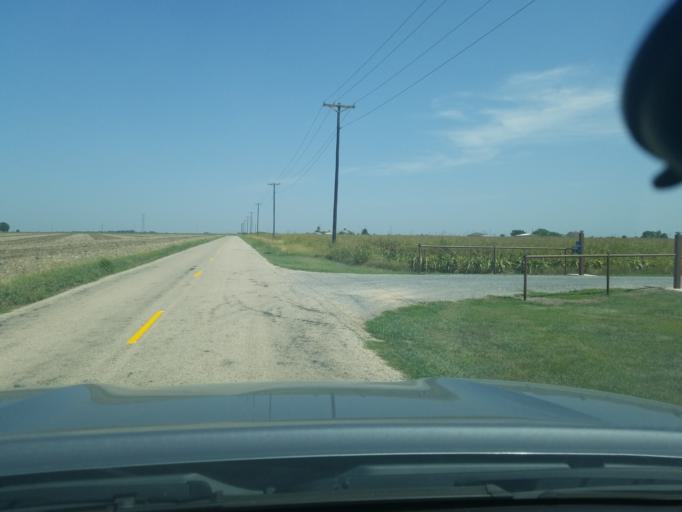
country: US
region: Texas
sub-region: Guadalupe County
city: Lake Dunlap
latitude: 29.6789
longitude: -98.0267
